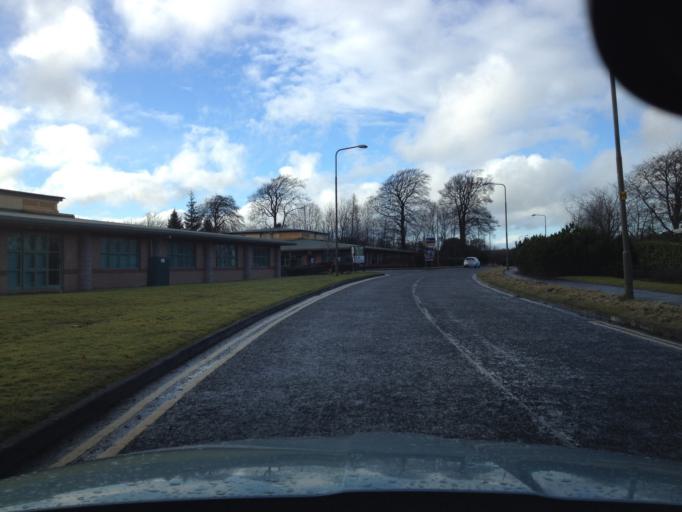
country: GB
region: Scotland
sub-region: West Lothian
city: Livingston
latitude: 55.8806
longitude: -3.5330
